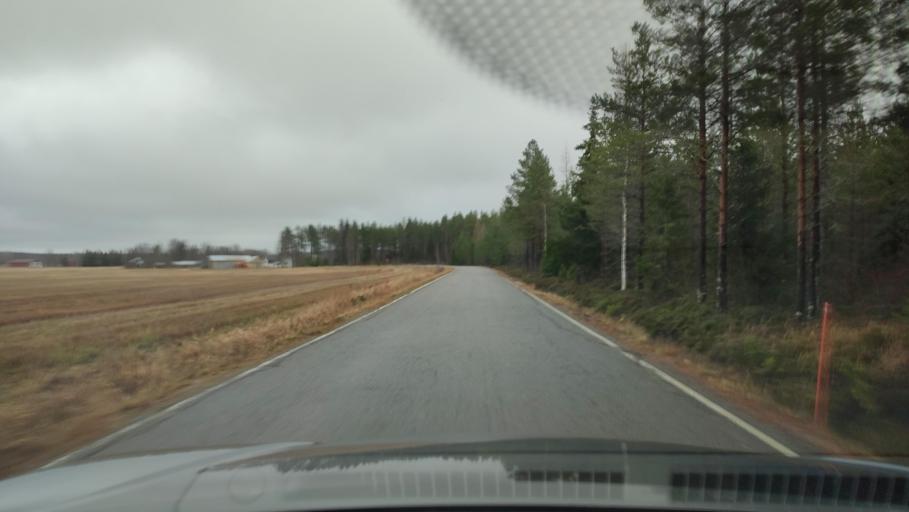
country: FI
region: Southern Ostrobothnia
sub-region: Suupohja
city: Isojoki
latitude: 62.1746
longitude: 21.9023
